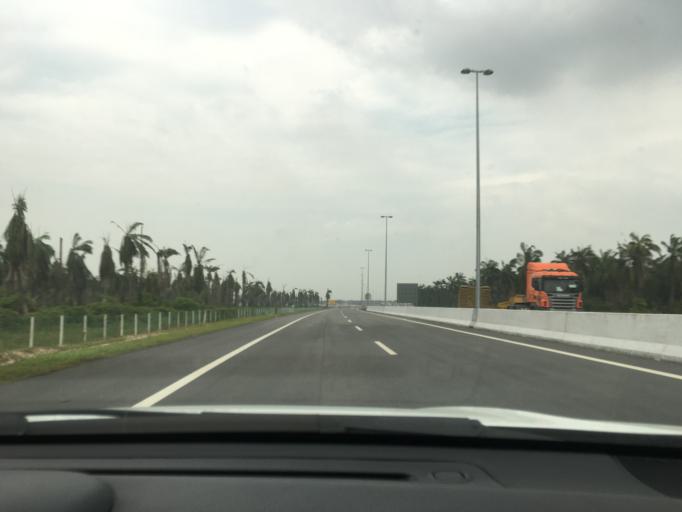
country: MY
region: Selangor
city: Klang
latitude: 3.1022
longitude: 101.4206
